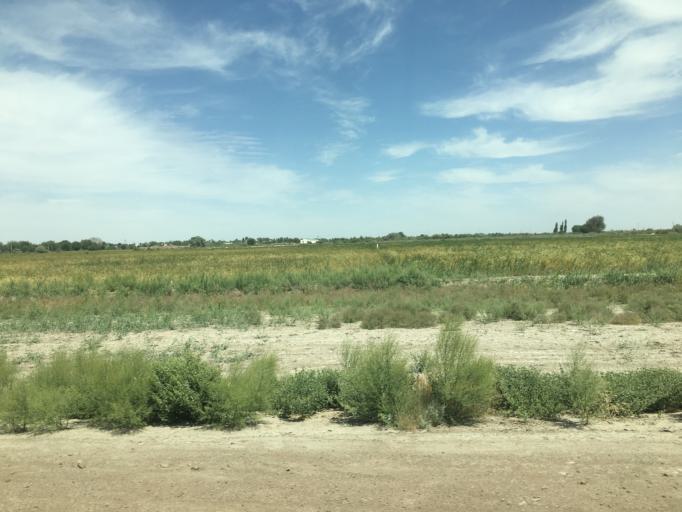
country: TM
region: Dasoguz
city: Dasoguz
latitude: 41.7625
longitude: 59.9546
